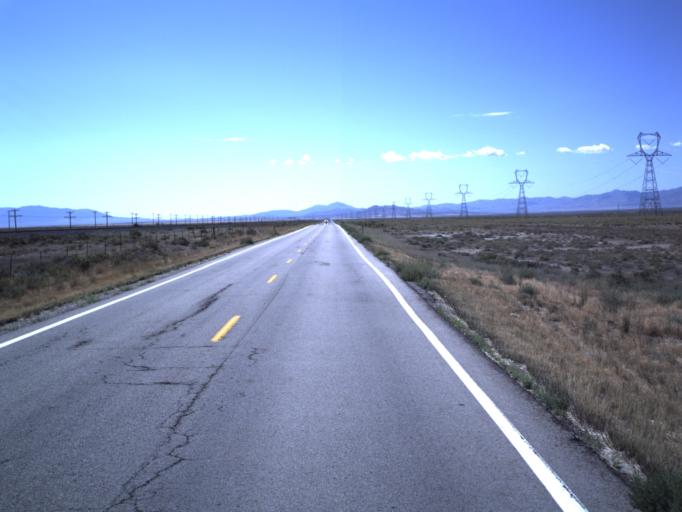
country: US
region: Utah
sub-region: Tooele County
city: Tooele
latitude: 40.3183
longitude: -112.4060
